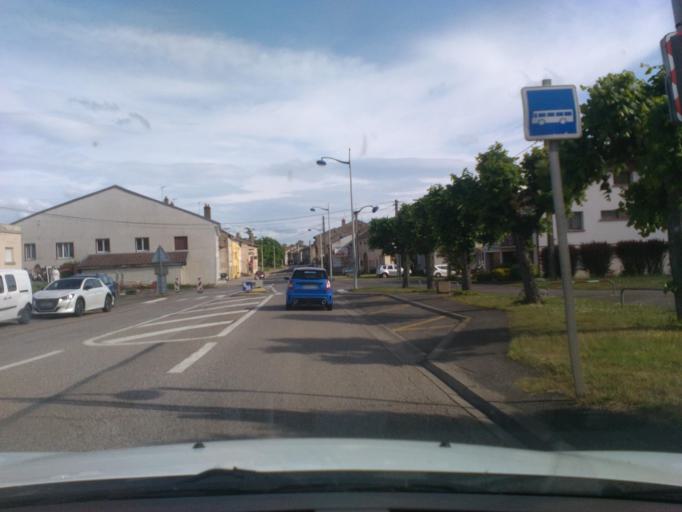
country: FR
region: Lorraine
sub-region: Departement de Meurthe-et-Moselle
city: Baccarat
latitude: 48.4877
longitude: 6.6948
